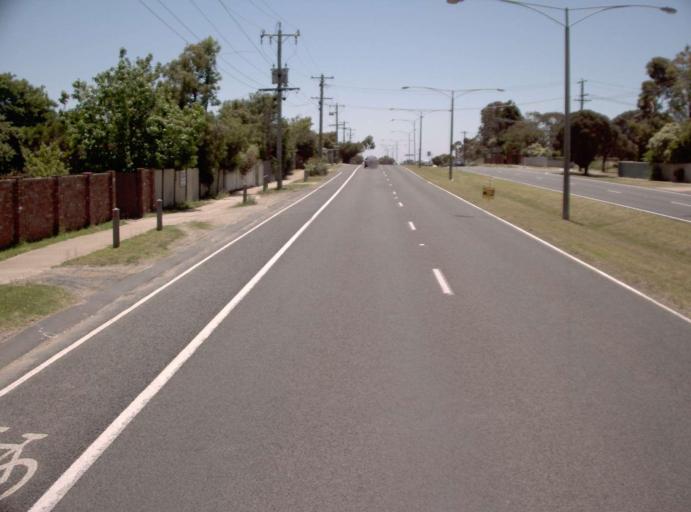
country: AU
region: Victoria
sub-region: Mornington Peninsula
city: Mornington
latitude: -38.2428
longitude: 145.0369
